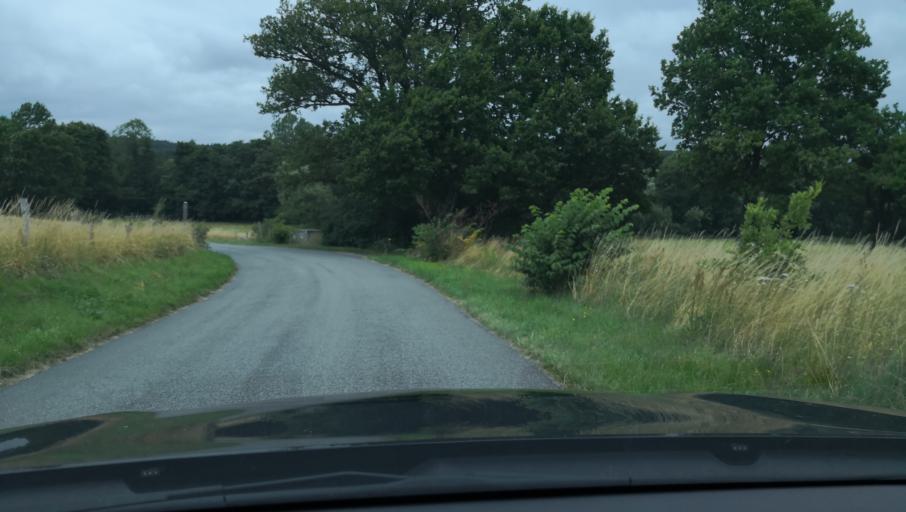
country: SE
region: Skane
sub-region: Simrishamns Kommun
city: Kivik
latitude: 55.7191
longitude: 14.1571
